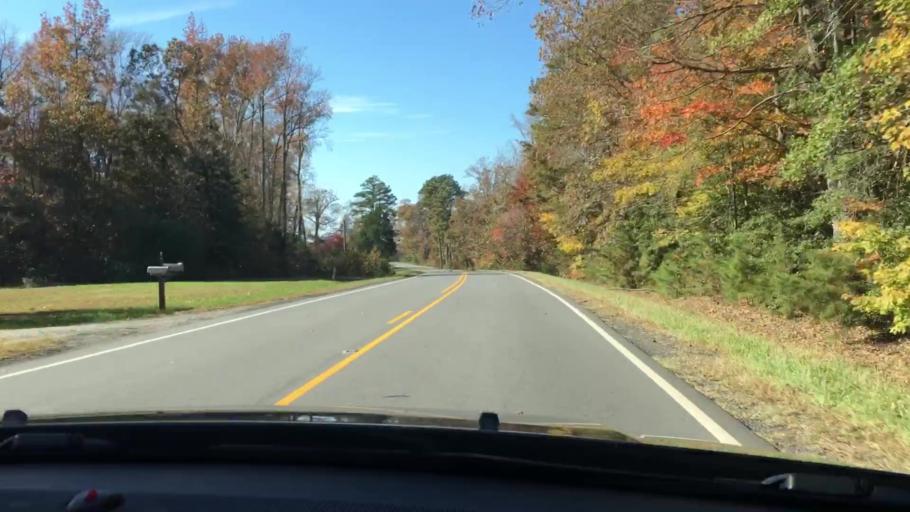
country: US
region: Virginia
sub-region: King William County
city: King William
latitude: 37.6749
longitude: -76.9831
